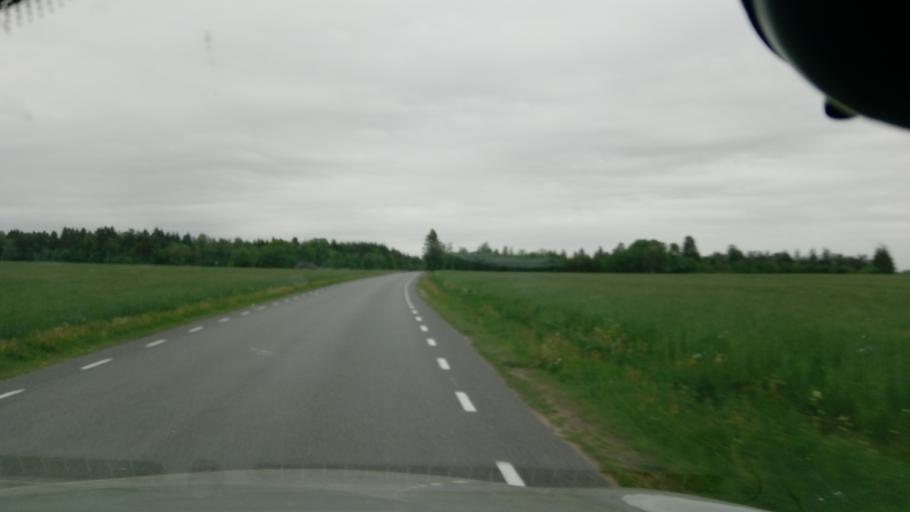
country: EE
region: Jaervamaa
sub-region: Koeru vald
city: Koeru
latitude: 58.9924
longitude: 26.0590
